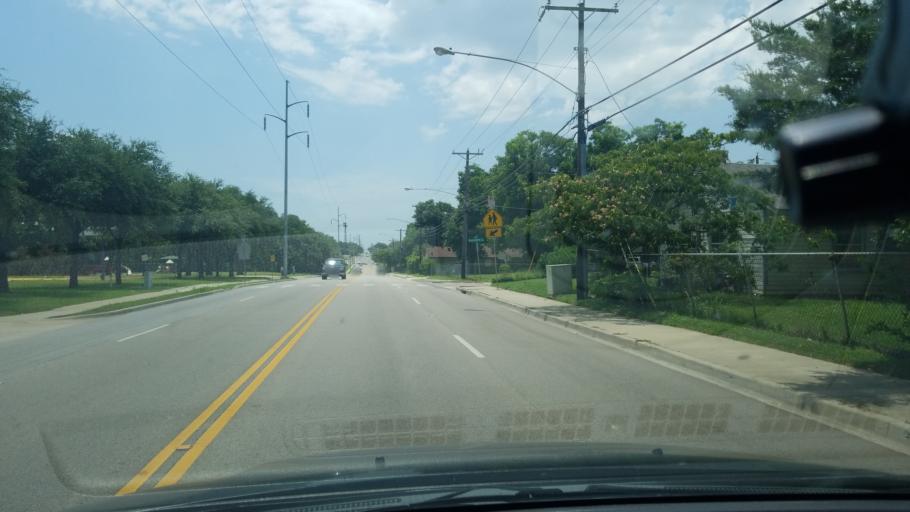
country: US
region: Texas
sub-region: Dallas County
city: Balch Springs
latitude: 32.7387
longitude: -96.6569
